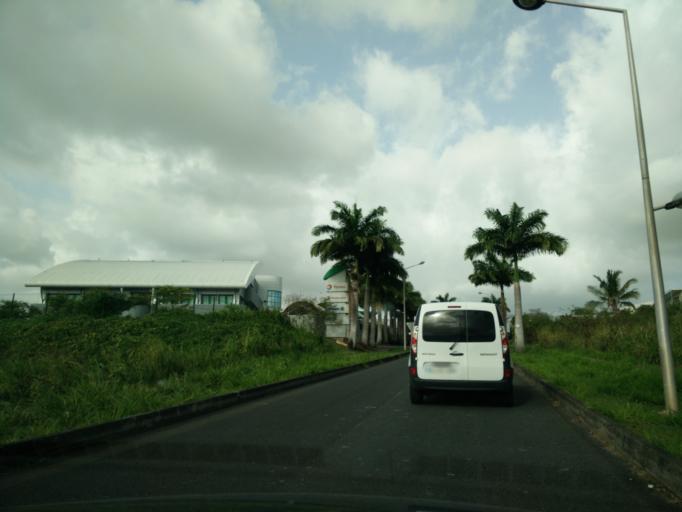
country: GP
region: Guadeloupe
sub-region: Guadeloupe
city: Baie-Mahault
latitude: 16.2385
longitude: -61.5738
